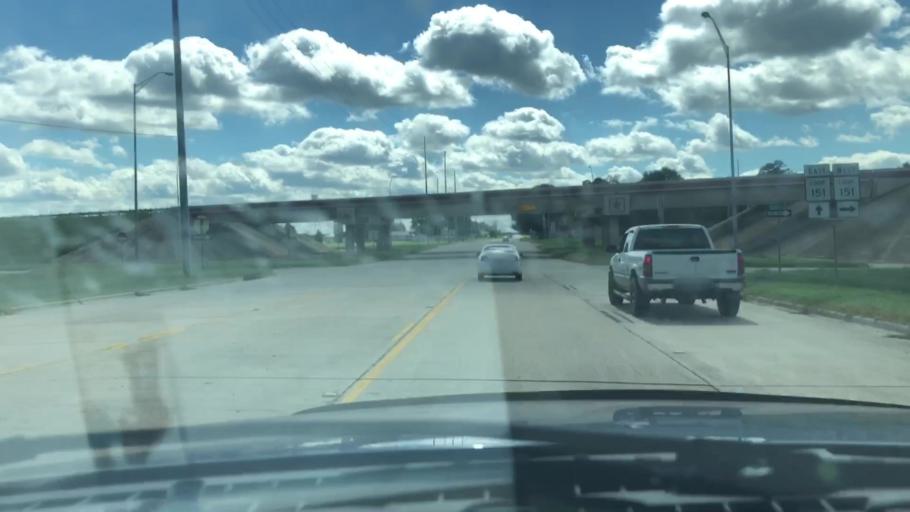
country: US
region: Texas
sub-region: Bowie County
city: Wake Village
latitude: 33.3877
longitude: -94.0922
